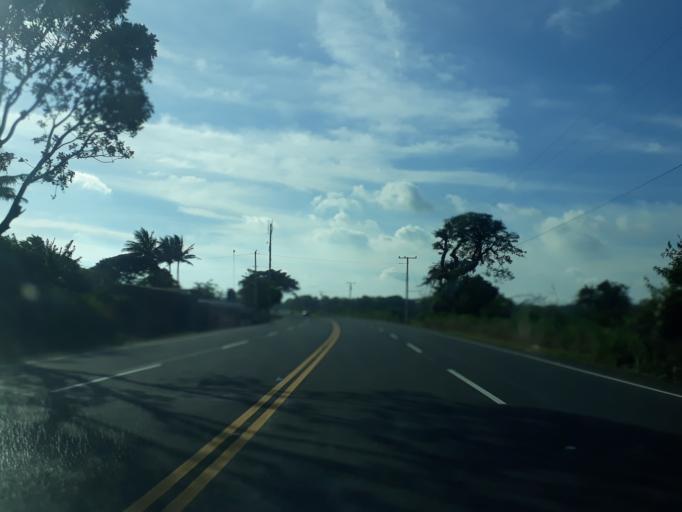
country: NI
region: Carazo
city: Diriamba
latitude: 11.9043
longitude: -86.2574
